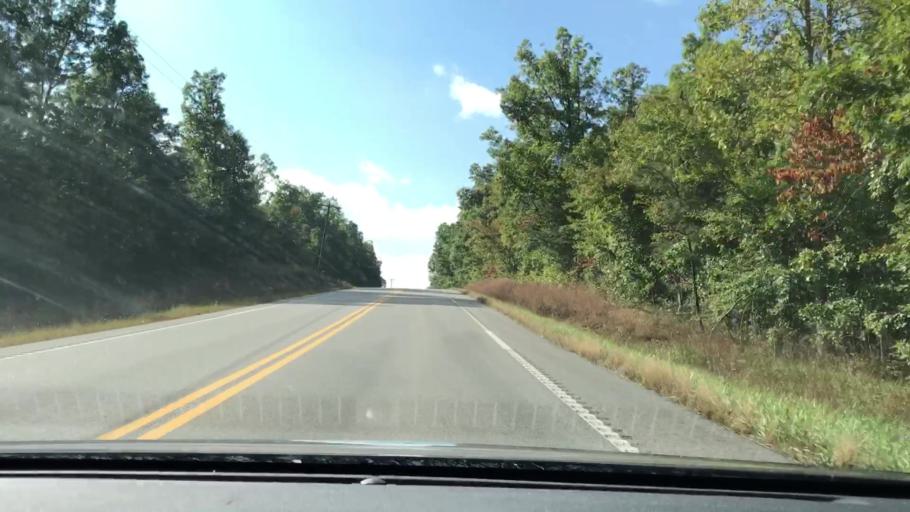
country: US
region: Tennessee
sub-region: Putnam County
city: Monterey
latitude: 36.1333
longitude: -85.2171
